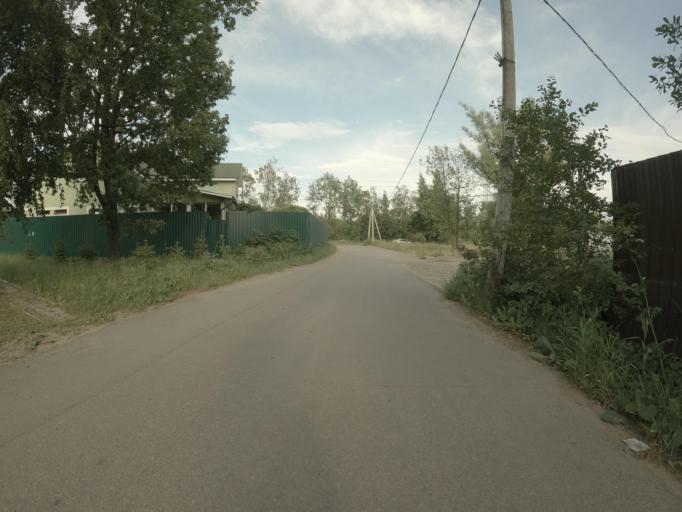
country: RU
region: St.-Petersburg
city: Krasnogvargeisky
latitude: 59.9355
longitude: 30.5195
